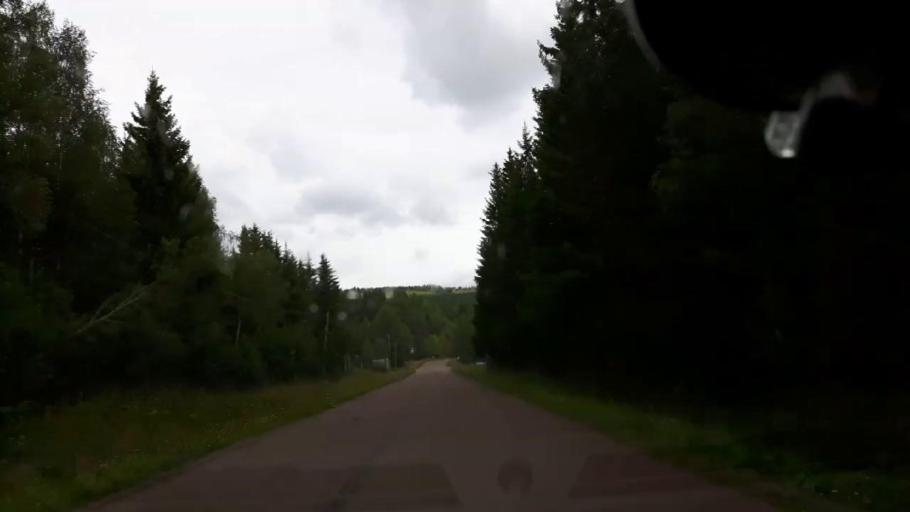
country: SE
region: Jaemtland
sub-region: Krokoms Kommun
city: Valla
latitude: 63.3906
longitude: 13.8759
